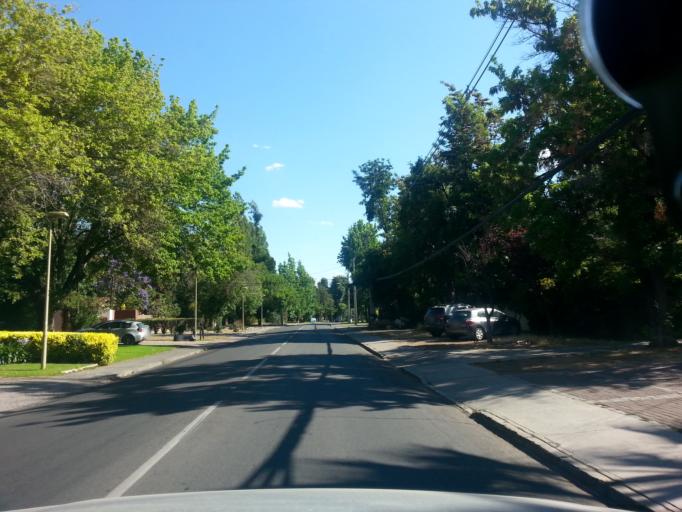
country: CL
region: Santiago Metropolitan
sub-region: Provincia de Santiago
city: Villa Presidente Frei, Nunoa, Santiago, Chile
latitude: -33.3971
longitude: -70.5315
